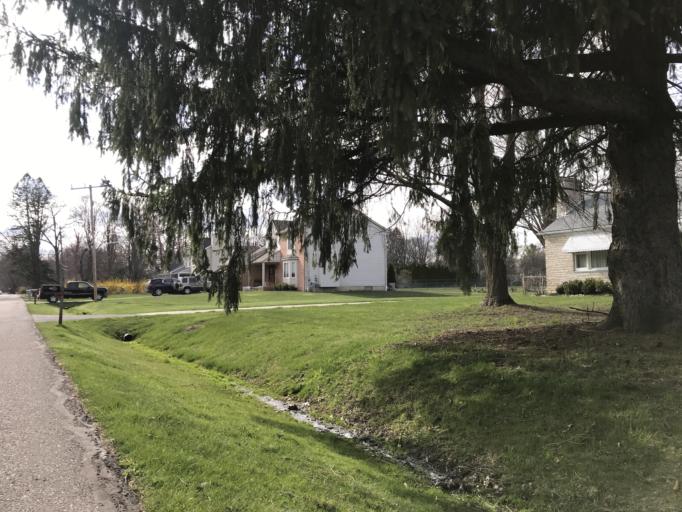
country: US
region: Michigan
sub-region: Oakland County
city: Farmington
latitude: 42.4666
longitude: -83.3400
